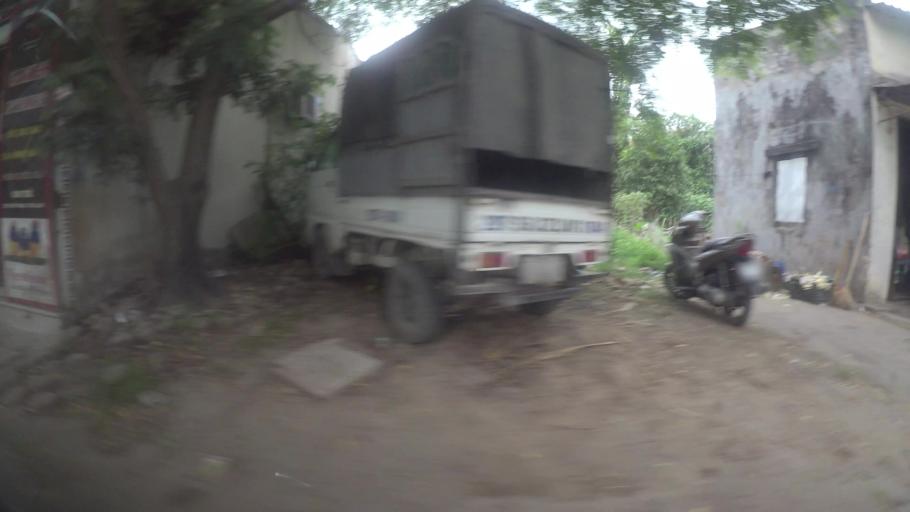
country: VN
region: Ha Noi
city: Cau Dien
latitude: 21.0382
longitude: 105.7422
